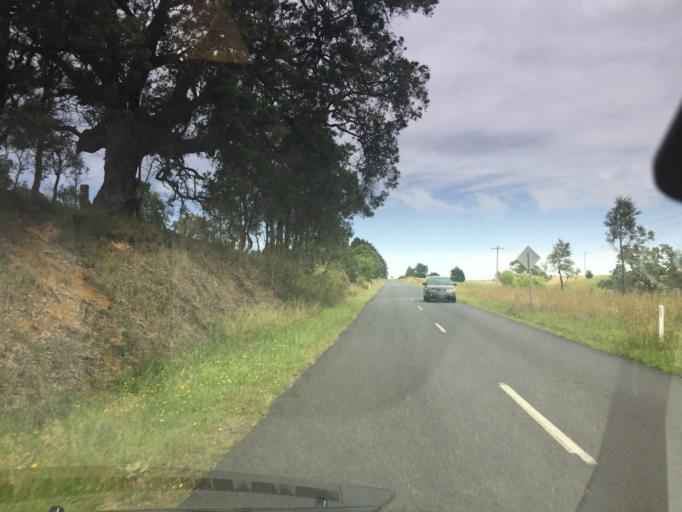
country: AU
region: New South Wales
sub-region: Bega Valley
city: Bega
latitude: -36.7400
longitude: 149.6467
